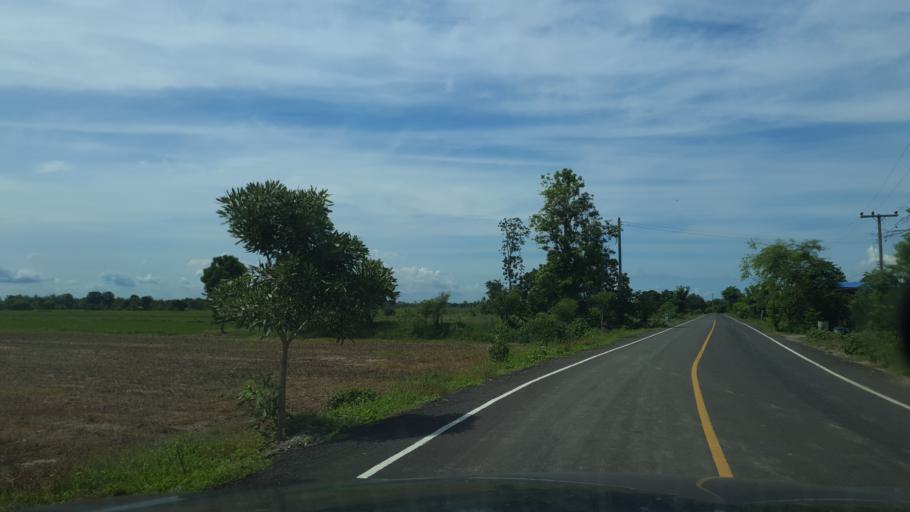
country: TH
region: Sukhothai
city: Si Samrong
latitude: 17.1944
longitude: 99.7379
